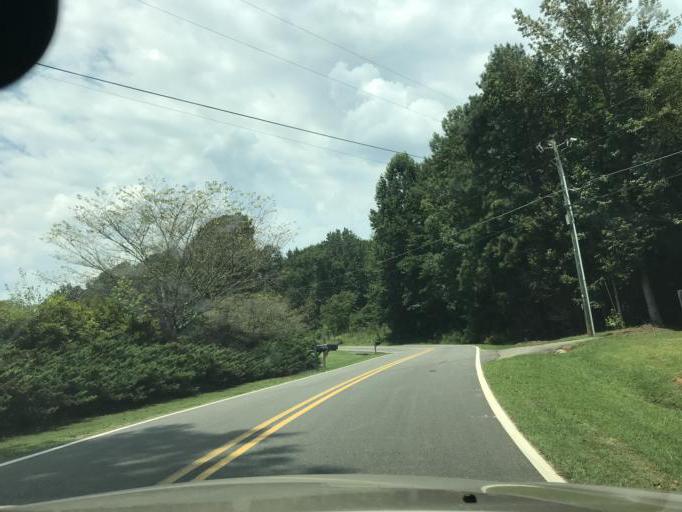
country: US
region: Georgia
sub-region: Dawson County
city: Dawsonville
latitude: 34.3310
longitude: -84.1992
